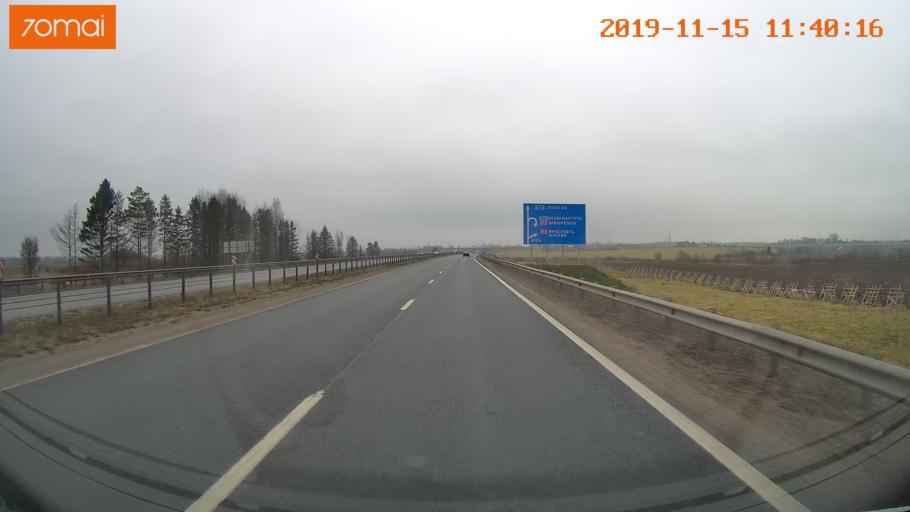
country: RU
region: Vologda
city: Molochnoye
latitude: 59.2124
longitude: 39.7469
